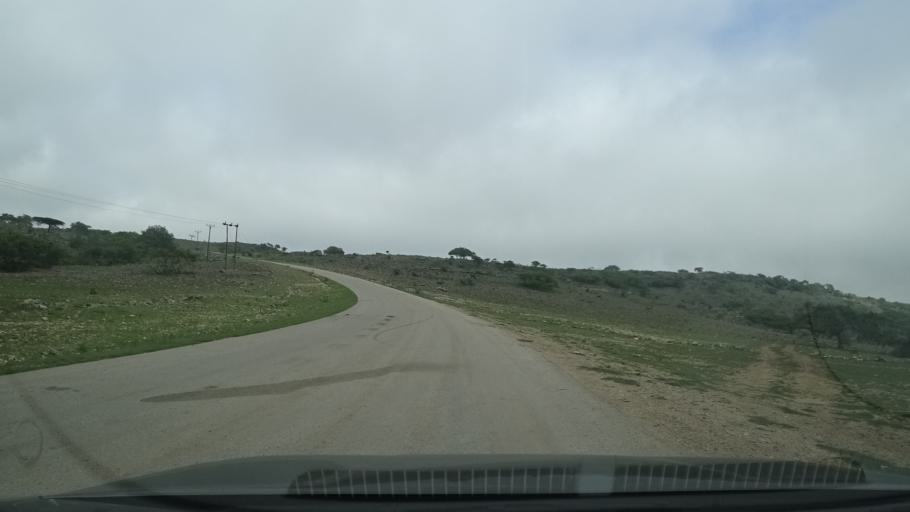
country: OM
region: Zufar
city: Salalah
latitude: 17.1214
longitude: 54.5900
